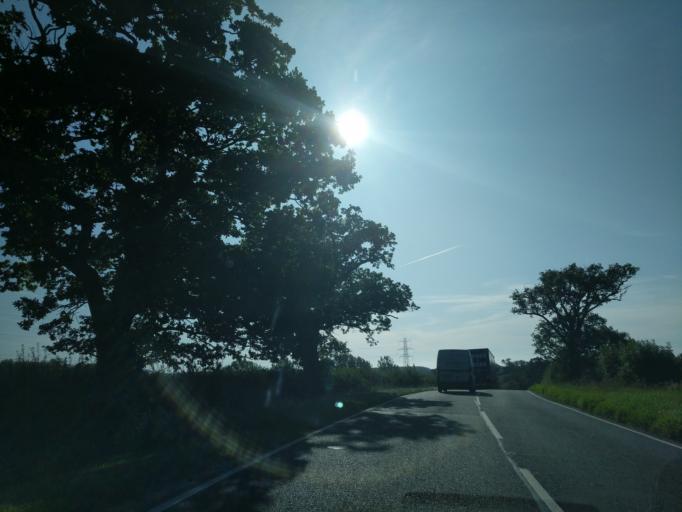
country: GB
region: England
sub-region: Lincolnshire
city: Bourne
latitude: 52.8020
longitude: -0.4557
